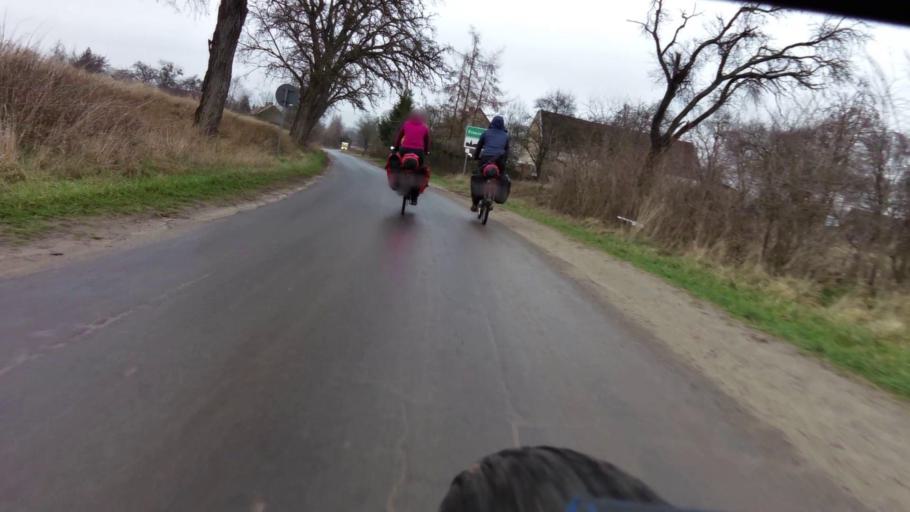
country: PL
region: Lubusz
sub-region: Powiat gorzowski
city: Kostrzyn nad Odra
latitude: 52.6488
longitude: 14.7161
